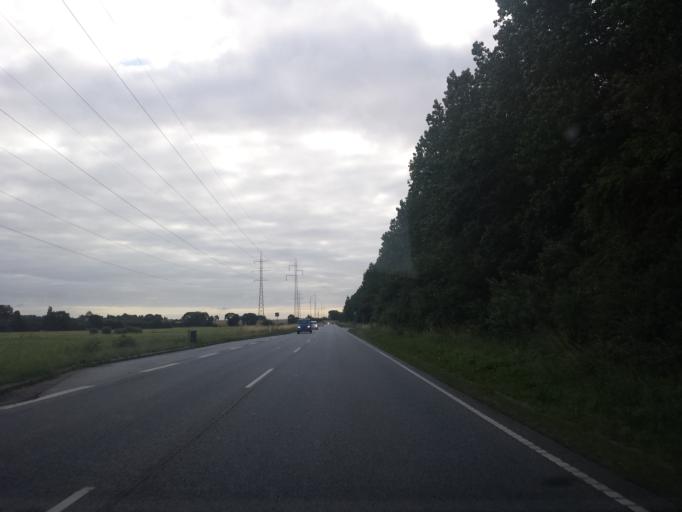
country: DK
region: South Denmark
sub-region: Sonderborg Kommune
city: Sonderborg
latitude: 54.9284
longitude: 9.7927
